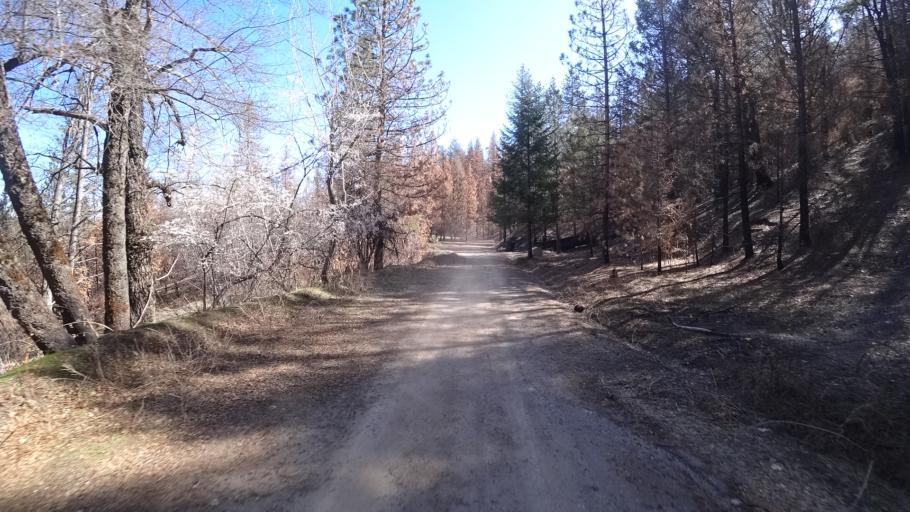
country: US
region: California
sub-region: Tehama County
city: Rancho Tehama Reserve
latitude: 39.6556
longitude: -122.7220
